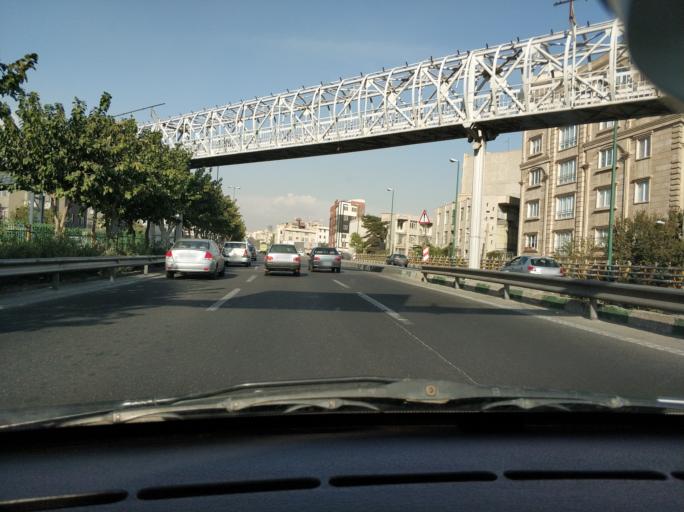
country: IR
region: Tehran
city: Tehran
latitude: 35.7158
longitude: 51.3550
